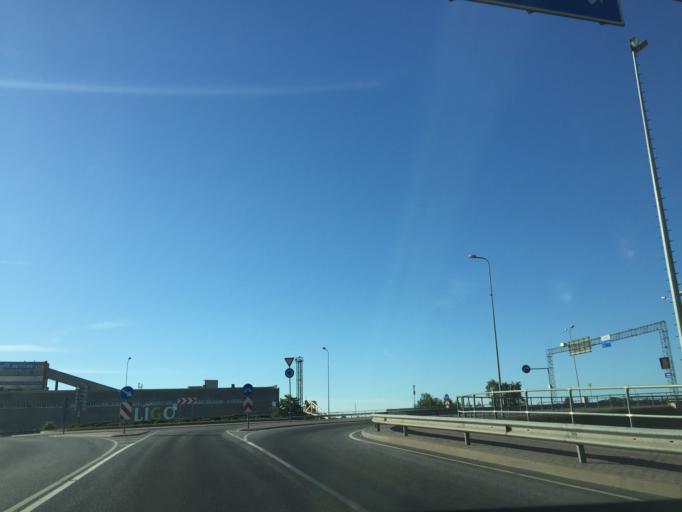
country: LV
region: Ventspils
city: Ventspils
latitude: 57.3902
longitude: 21.5902
